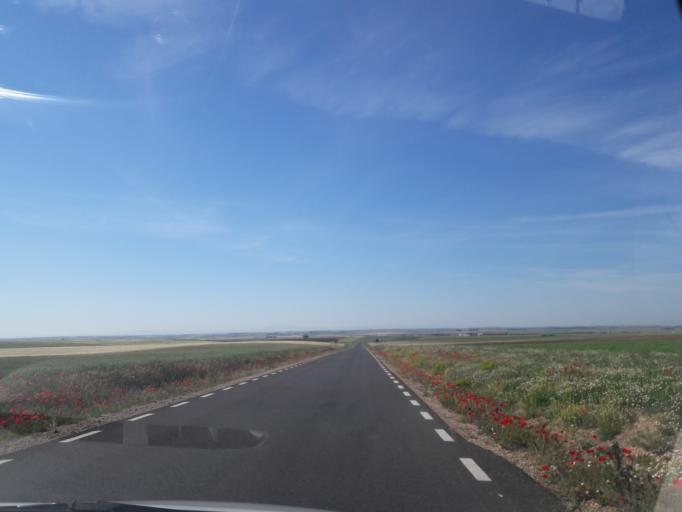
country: ES
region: Castille and Leon
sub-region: Provincia de Salamanca
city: Parada de Rubiales
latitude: 41.1444
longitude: -5.4320
